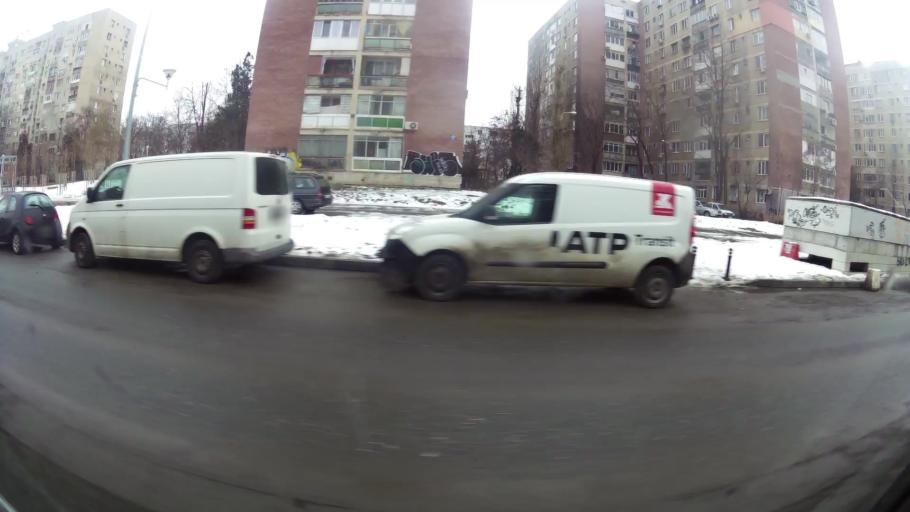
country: RO
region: Ilfov
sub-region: Comuna Chiajna
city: Rosu
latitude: 44.4194
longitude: 26.0202
